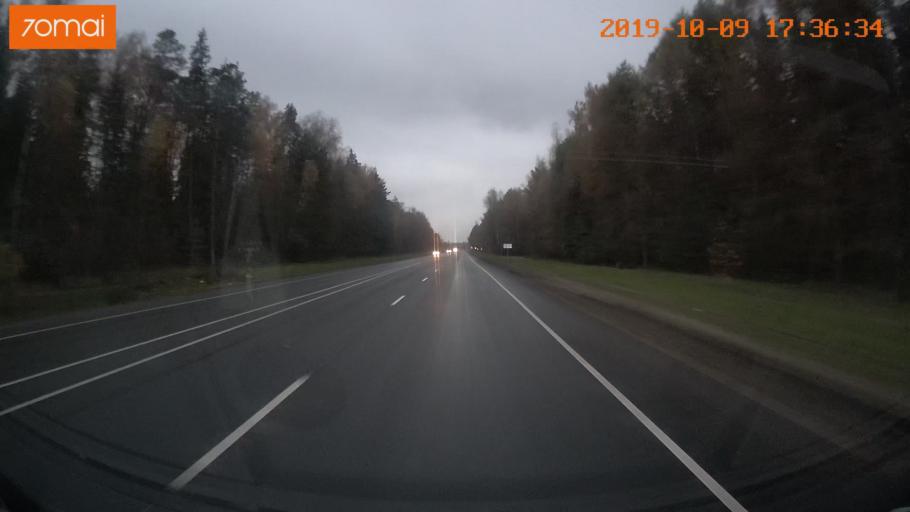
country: RU
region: Ivanovo
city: Bogorodskoye
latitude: 57.0767
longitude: 40.9956
